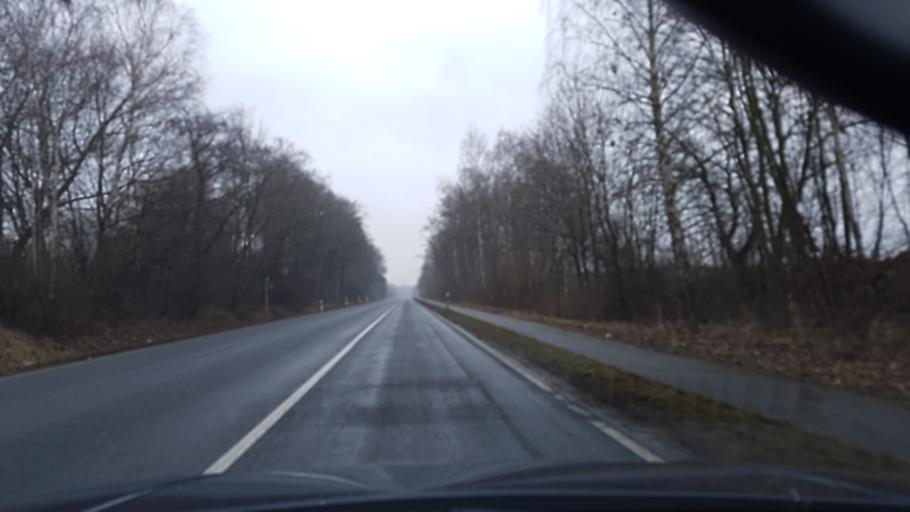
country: DE
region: Lower Saxony
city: Leiferde
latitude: 52.1914
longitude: 10.4568
